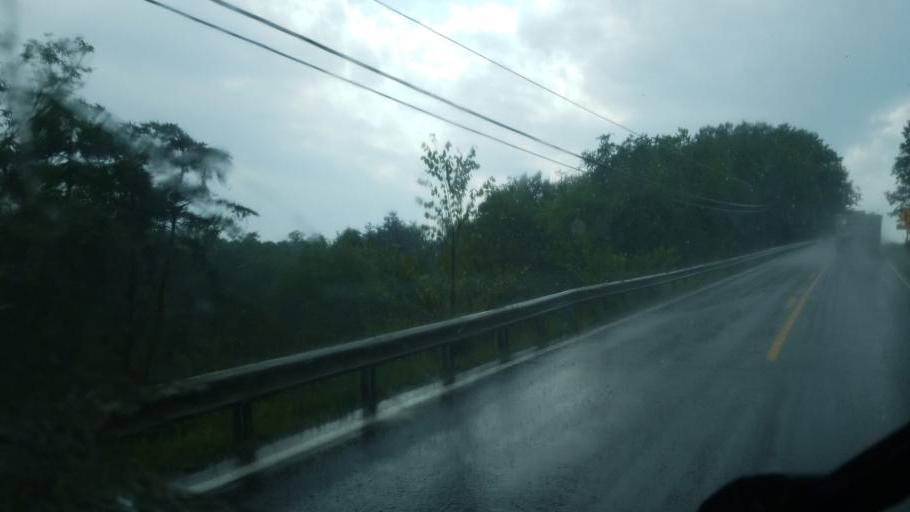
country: US
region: West Virginia
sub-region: Mineral County
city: Fort Ashby
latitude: 39.5416
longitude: -78.5972
